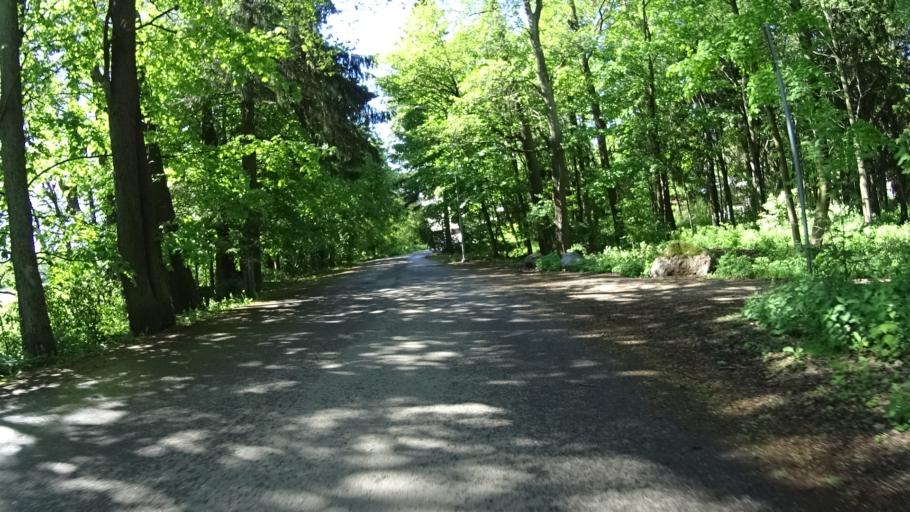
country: FI
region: Uusimaa
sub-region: Helsinki
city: Teekkarikylae
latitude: 60.1692
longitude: 24.8602
